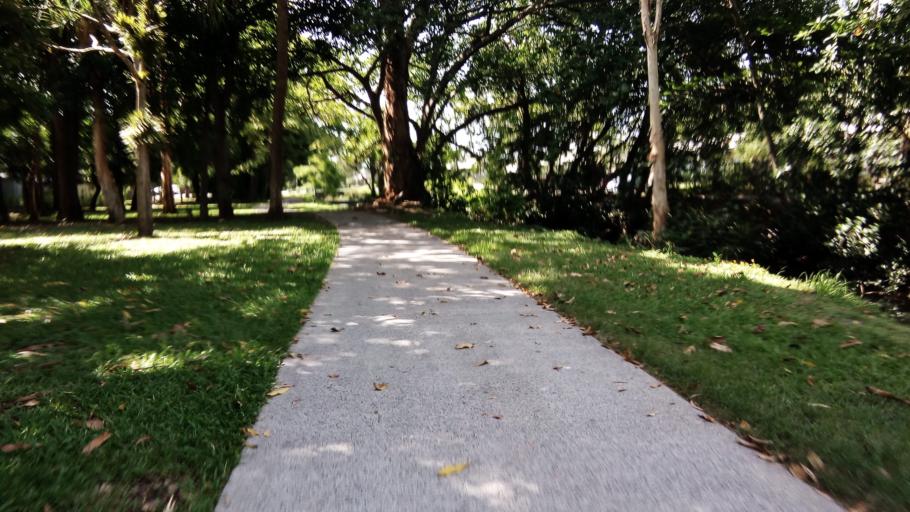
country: AU
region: Queensland
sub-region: Cairns
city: Cairns
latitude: -16.9146
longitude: 145.7618
